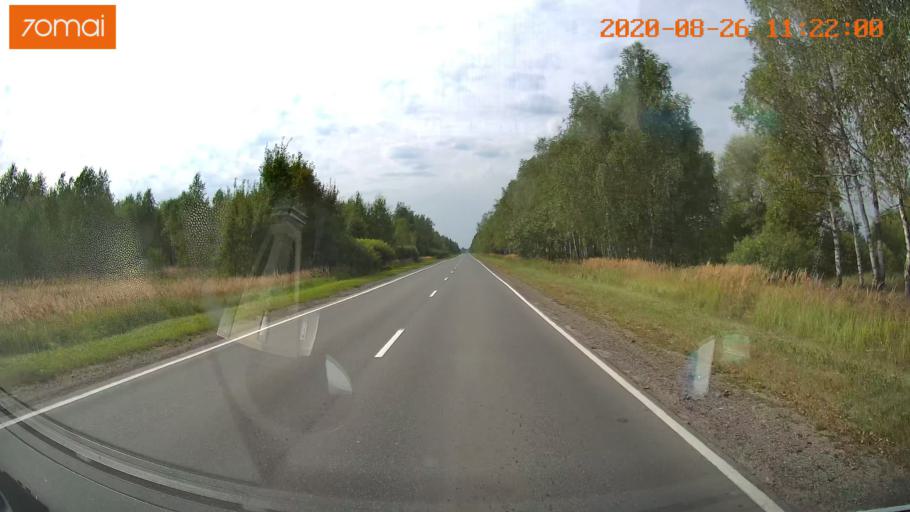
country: RU
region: Rjazan
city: Shilovo
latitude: 54.3693
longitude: 41.0349
